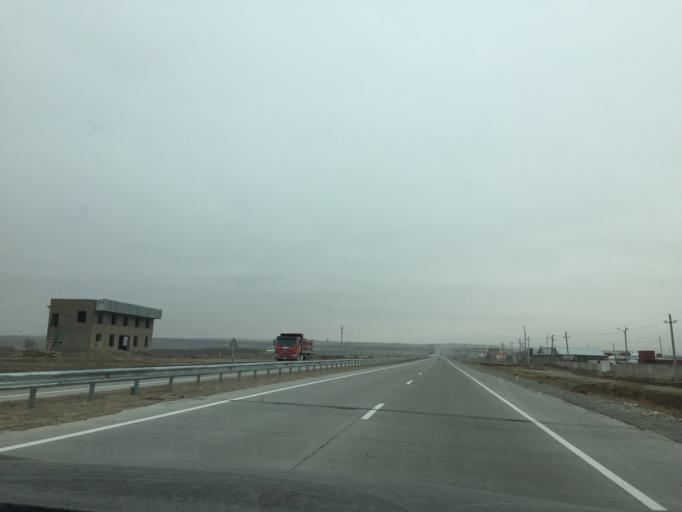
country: KZ
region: Ongtustik Qazaqstan
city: Aksu
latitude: 42.4746
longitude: 69.8212
